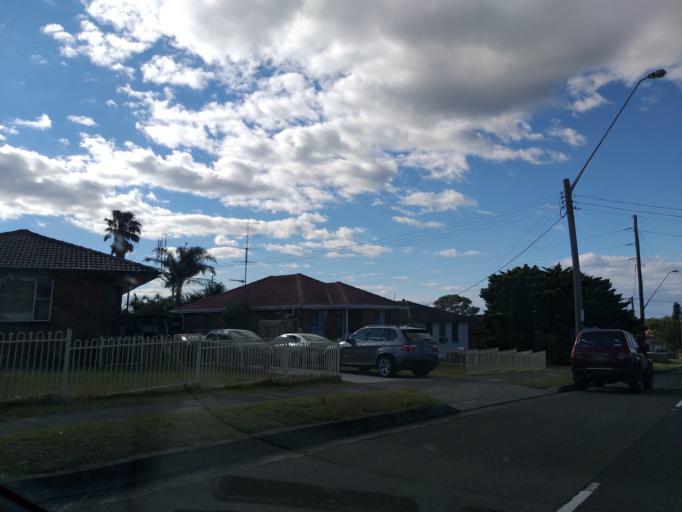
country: AU
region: New South Wales
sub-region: Shellharbour
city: Lake Illawarra
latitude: -34.5554
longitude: 150.8494
